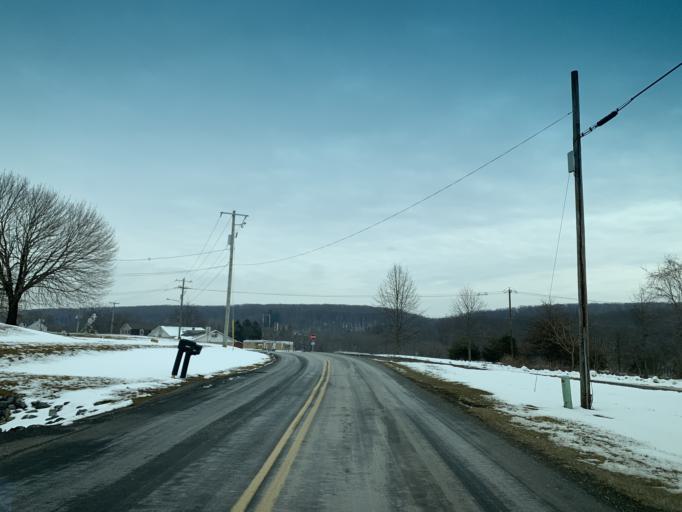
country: US
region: Pennsylvania
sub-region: York County
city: Susquehanna Trails
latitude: 39.7187
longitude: -76.3451
